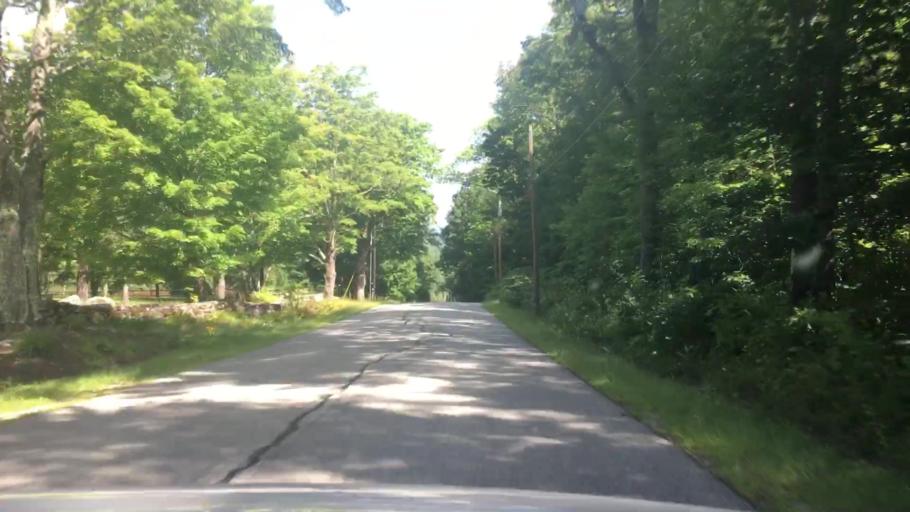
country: US
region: Maine
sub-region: Androscoggin County
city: Turner
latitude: 44.1891
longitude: -70.2604
